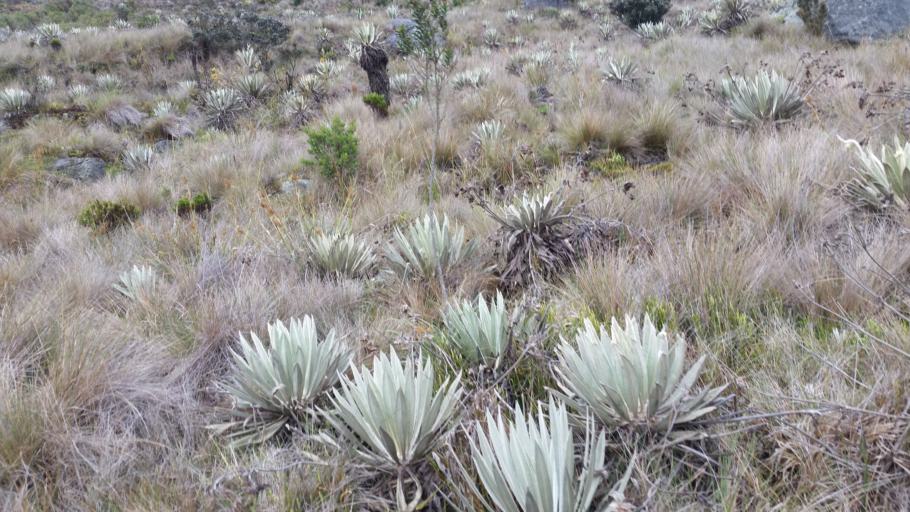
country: CO
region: Cundinamarca
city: Pasca
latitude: 4.3677
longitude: -74.2180
